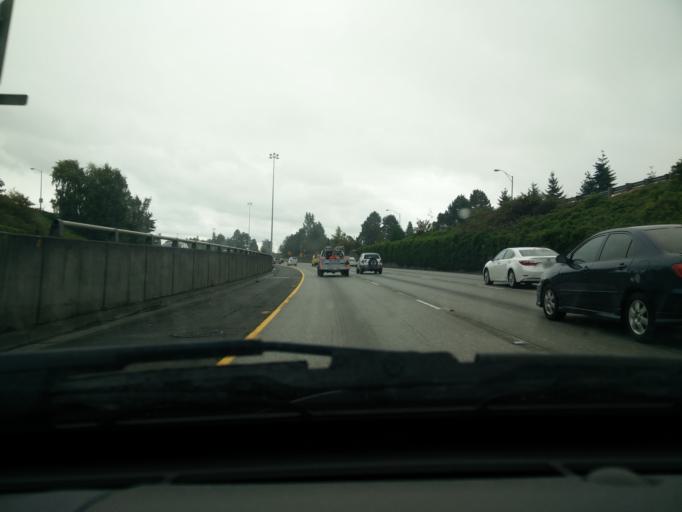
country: US
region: Washington
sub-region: King County
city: Shoreline
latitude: 47.6901
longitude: -122.3292
